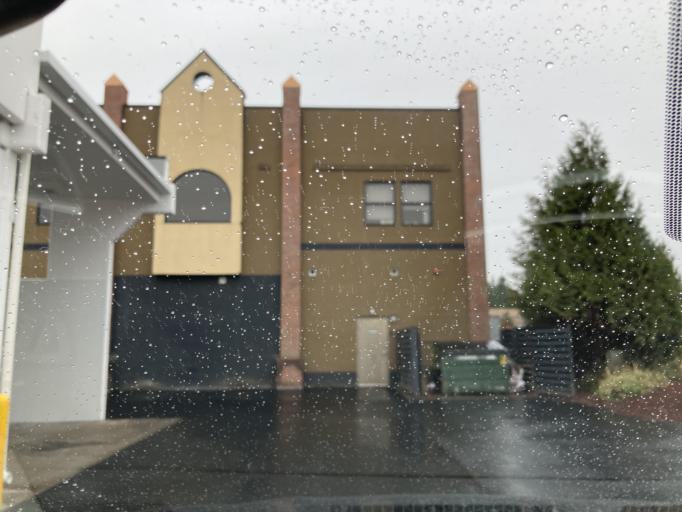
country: US
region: Washington
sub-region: Pierce County
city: Graham
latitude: 47.0860
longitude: -122.2951
